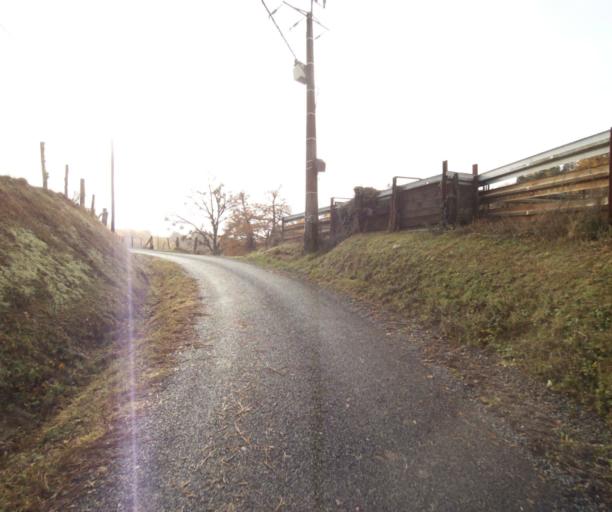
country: FR
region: Limousin
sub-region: Departement de la Correze
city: Cornil
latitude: 45.2268
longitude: 1.6396
